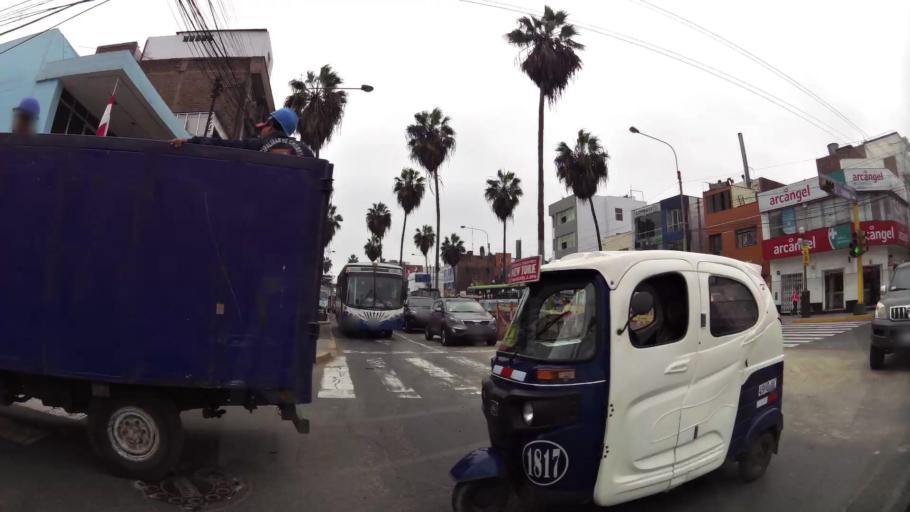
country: PE
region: Lima
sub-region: Lima
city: Surco
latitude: -12.1687
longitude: -77.0246
